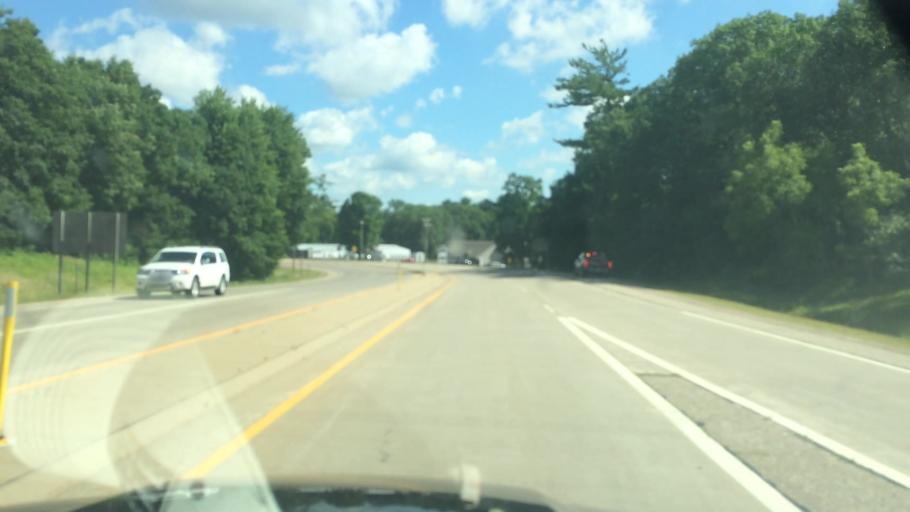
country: US
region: Wisconsin
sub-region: Waupaca County
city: Waupaca
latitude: 44.3394
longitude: -89.0692
